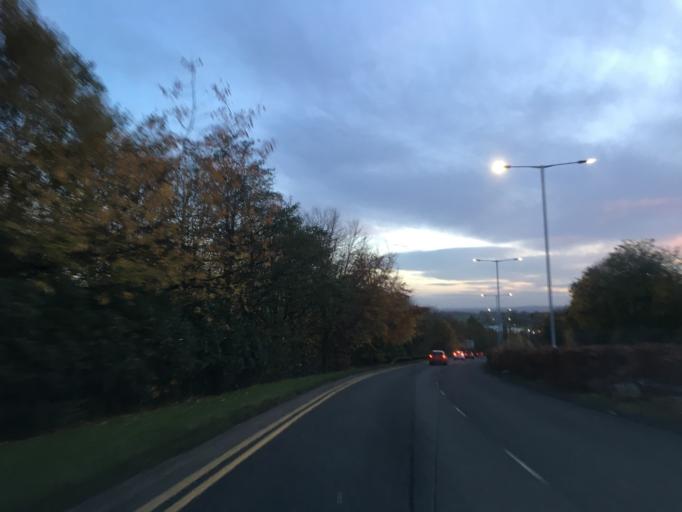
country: GB
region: Scotland
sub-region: Fife
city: Dunfermline
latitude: 56.0712
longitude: -3.4515
